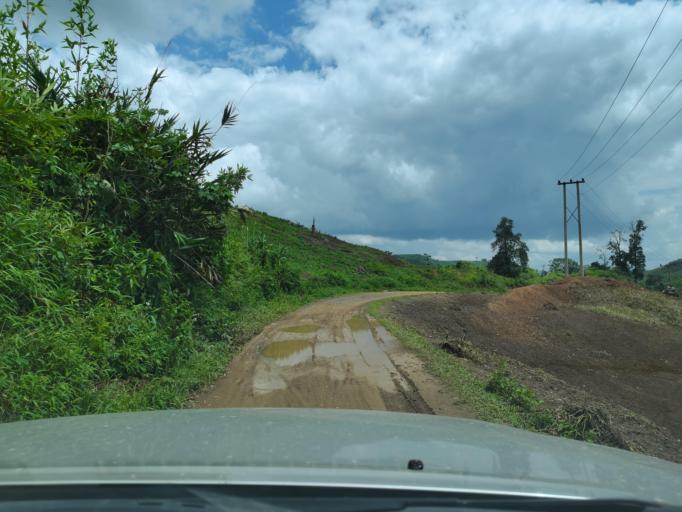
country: LA
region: Loungnamtha
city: Muang Long
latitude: 20.7319
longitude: 101.0145
